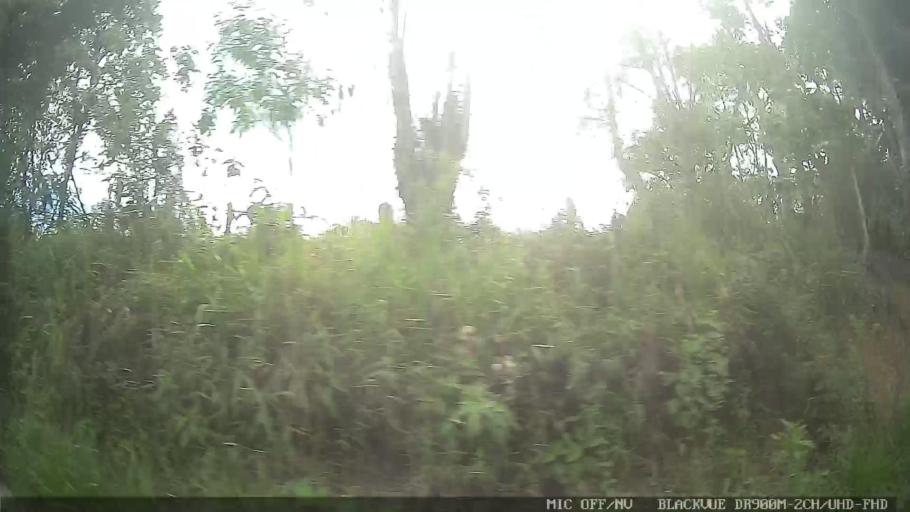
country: BR
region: Minas Gerais
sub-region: Extrema
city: Extrema
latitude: -22.7674
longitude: -46.3201
